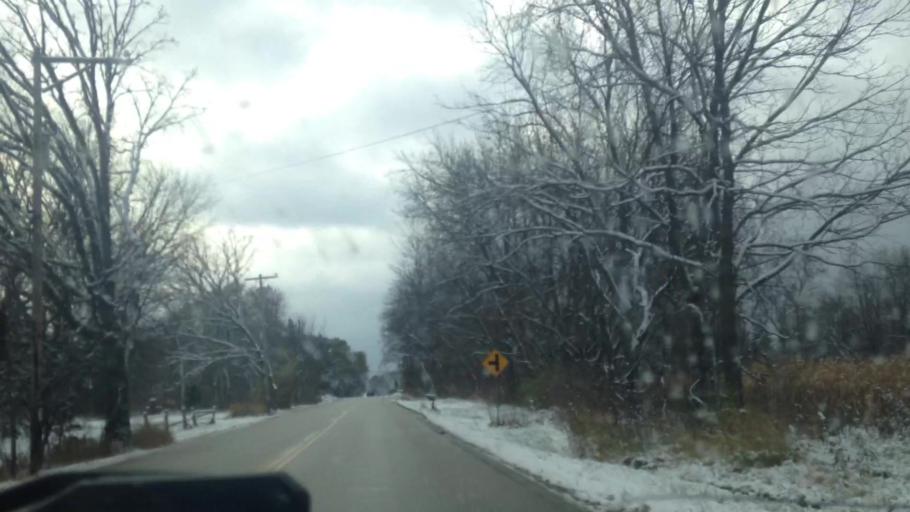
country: US
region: Wisconsin
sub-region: Waukesha County
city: Lannon
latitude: 43.1719
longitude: -88.1831
